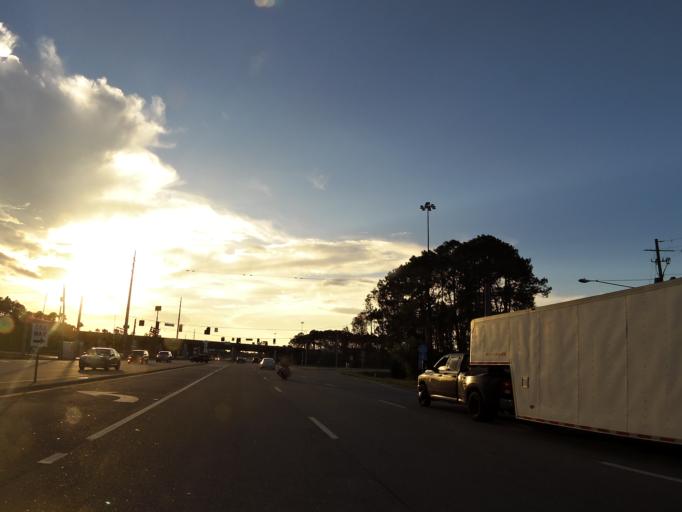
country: US
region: Georgia
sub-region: Camden County
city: Kingsland
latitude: 30.7898
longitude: -81.6560
